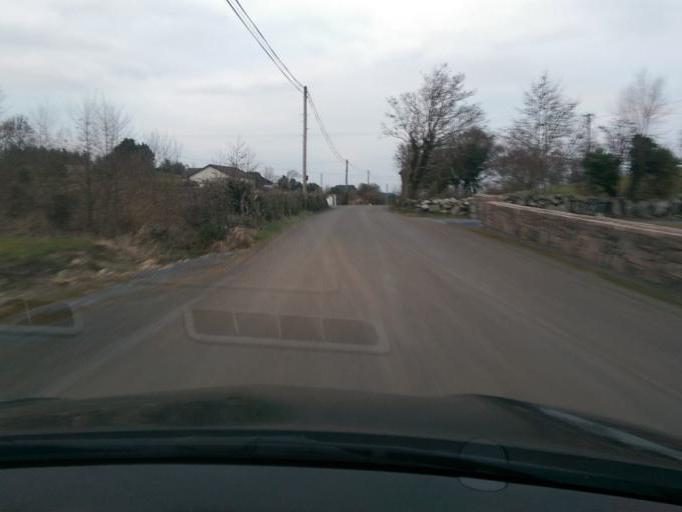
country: IE
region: Connaught
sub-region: County Galway
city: Bearna
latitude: 53.2941
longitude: -9.1631
